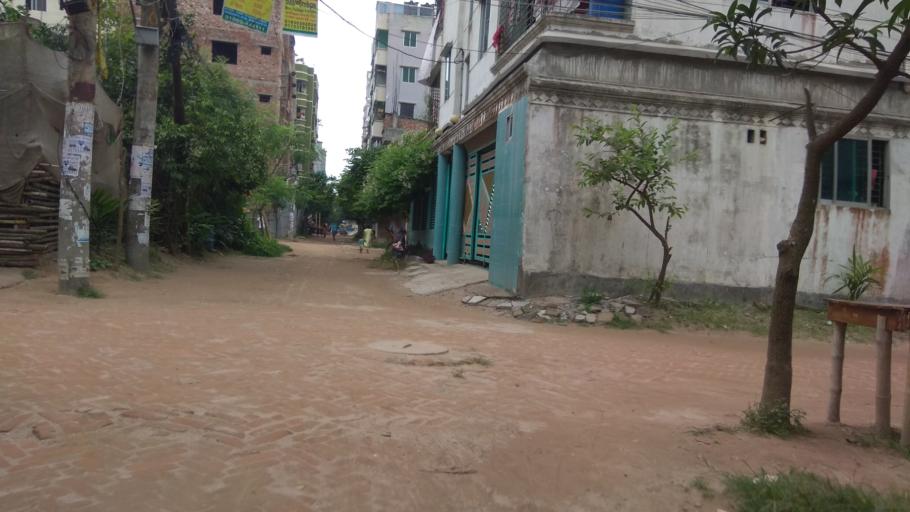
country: BD
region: Dhaka
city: Tungi
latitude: 23.8218
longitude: 90.3520
